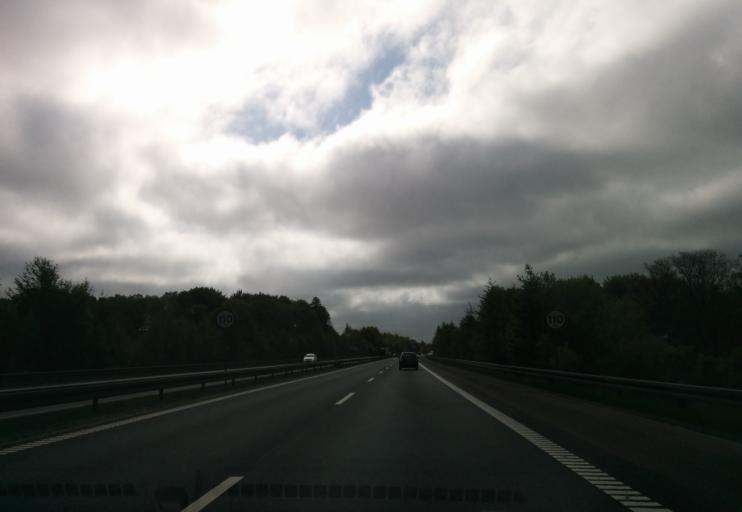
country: DK
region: South Denmark
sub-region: Fredericia Kommune
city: Taulov
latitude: 55.5591
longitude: 9.6265
